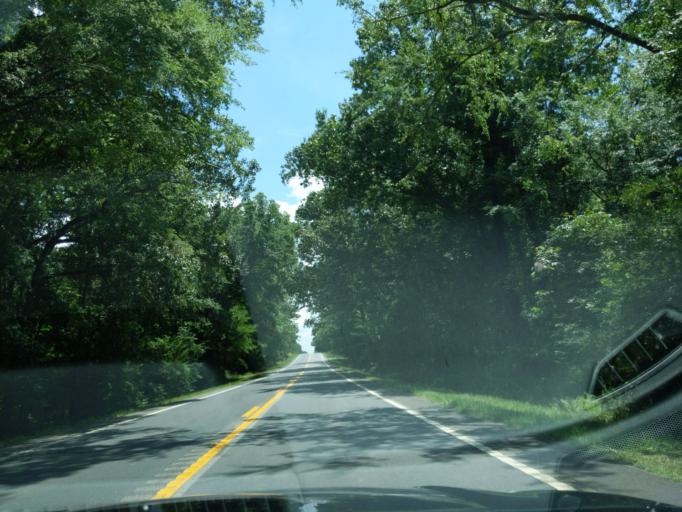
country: US
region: South Carolina
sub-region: Edgefield County
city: Edgefield
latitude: 33.8477
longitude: -81.9786
